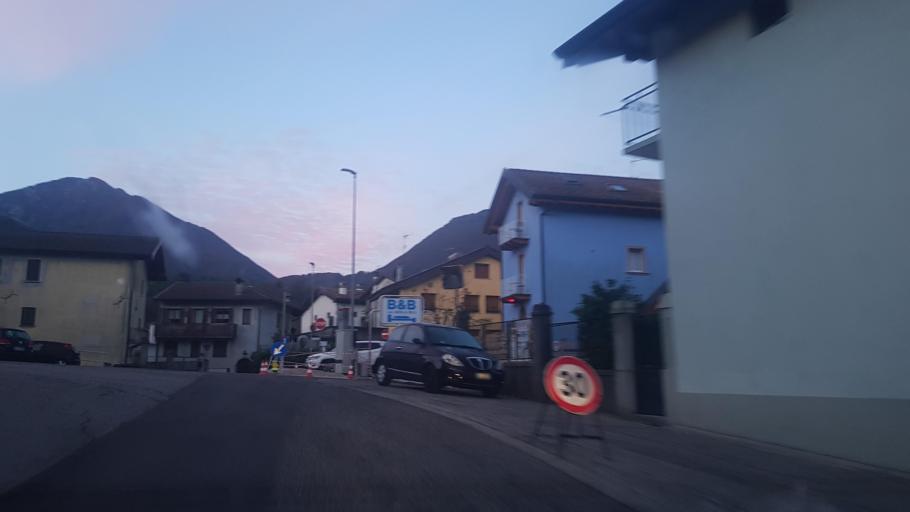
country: IT
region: Friuli Venezia Giulia
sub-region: Provincia di Udine
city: Chiaulis
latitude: 46.3886
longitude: 12.9928
